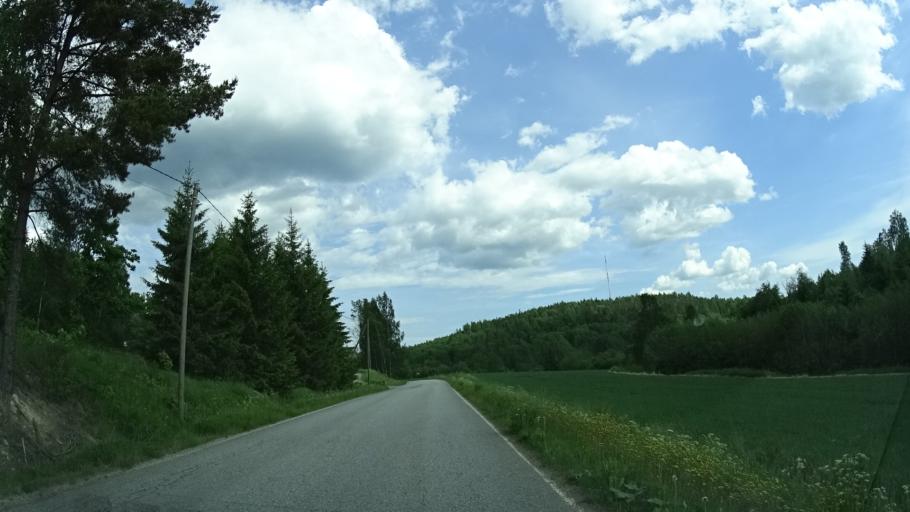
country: FI
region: Uusimaa
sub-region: Helsinki
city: Siuntio
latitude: 60.1969
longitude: 24.2268
